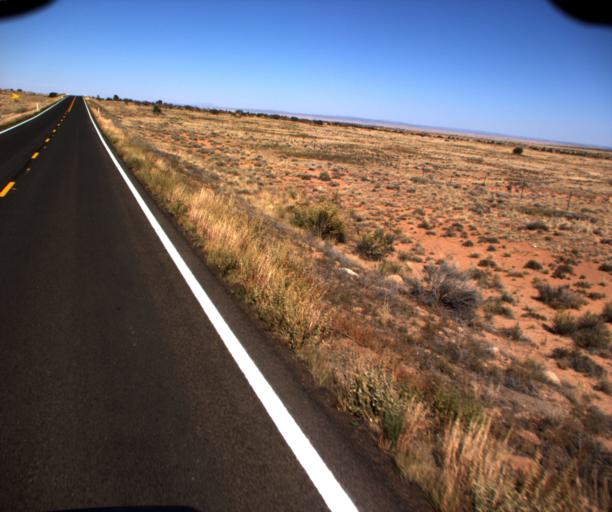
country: US
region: Arizona
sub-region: Coconino County
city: Tuba City
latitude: 35.9216
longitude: -110.8870
